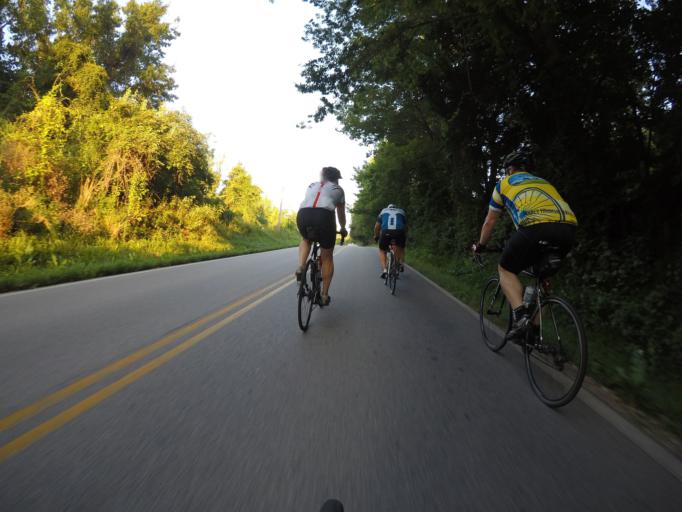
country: US
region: Kansas
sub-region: Leavenworth County
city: Lansing
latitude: 39.2160
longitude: -94.8488
